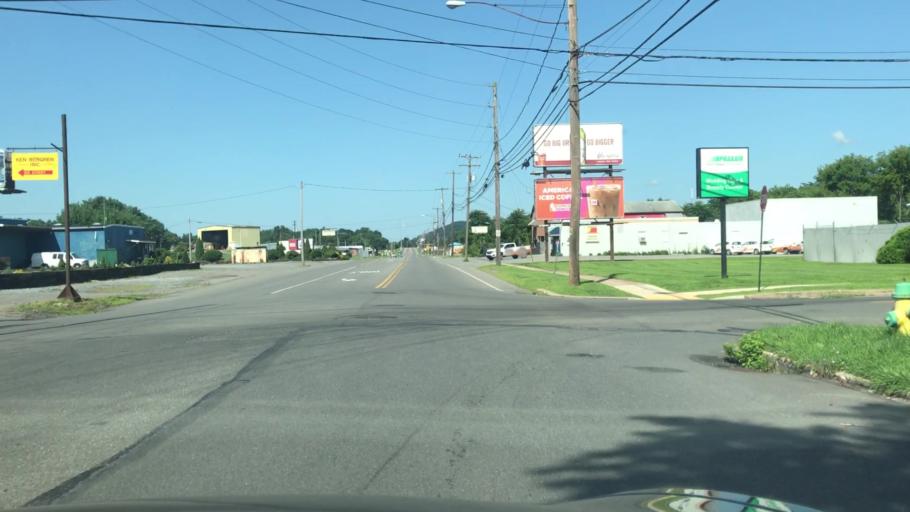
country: US
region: Pennsylvania
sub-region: Lycoming County
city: Duboistown
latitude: 41.2373
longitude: -77.0321
